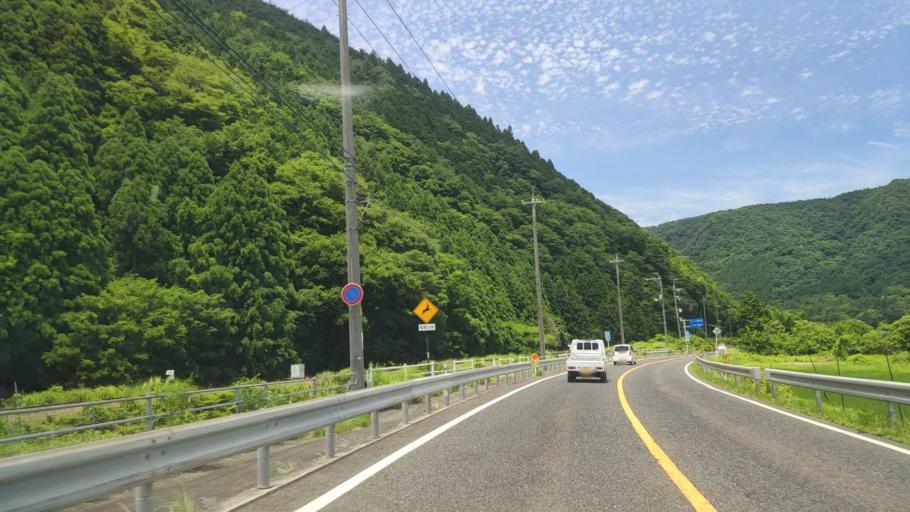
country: JP
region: Tottori
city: Tottori
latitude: 35.3607
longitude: 134.3785
